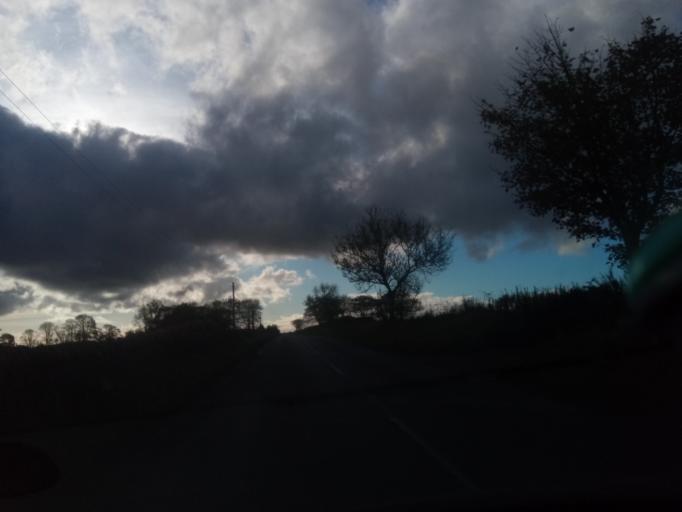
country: GB
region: Scotland
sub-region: The Scottish Borders
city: Chirnside
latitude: 55.8041
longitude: -2.1956
